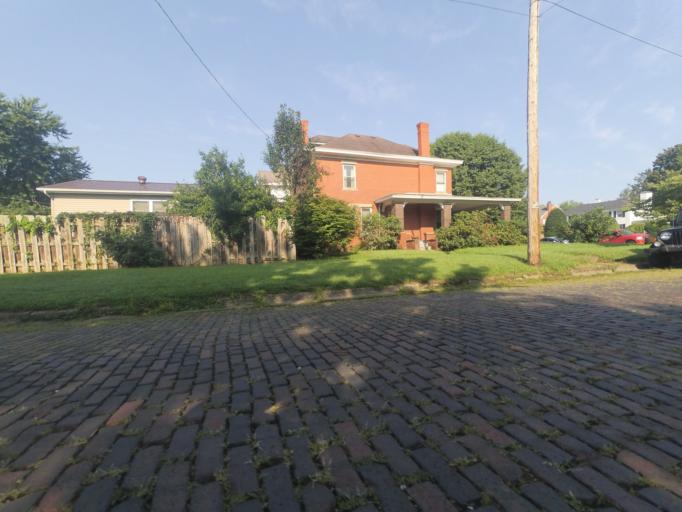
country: US
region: West Virginia
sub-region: Cabell County
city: Huntington
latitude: 38.4098
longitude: -82.4461
